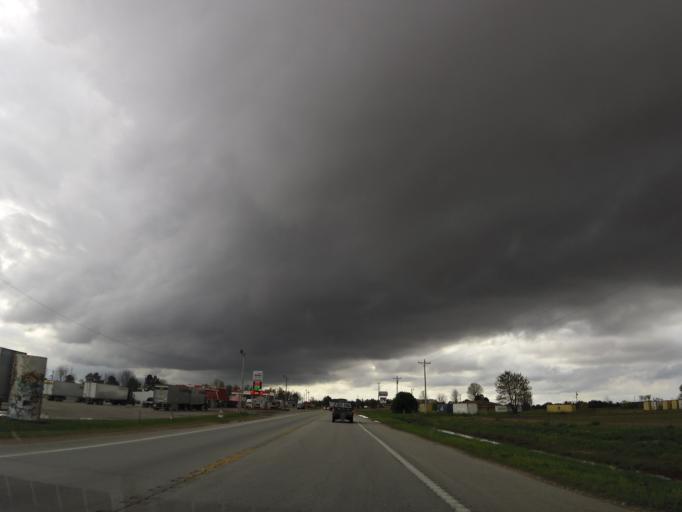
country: US
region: Arkansas
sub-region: Clay County
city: Corning
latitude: 36.5014
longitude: -90.5399
